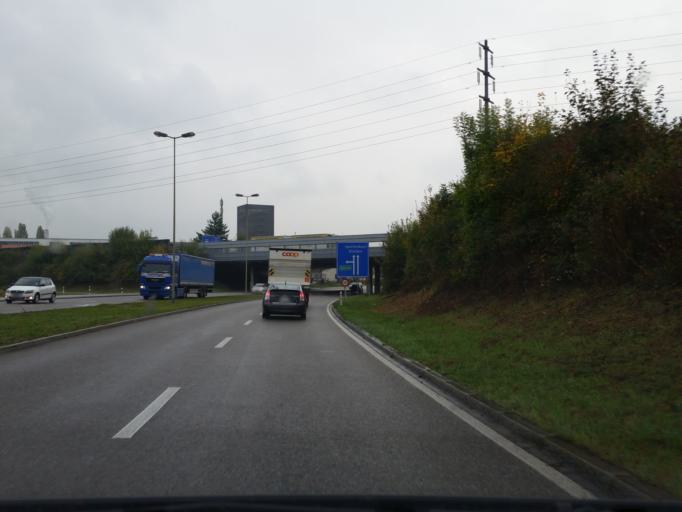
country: CH
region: Zurich
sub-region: Bezirk Dietikon
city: Dietikon / Vorstadt
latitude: 47.4235
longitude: 8.3914
